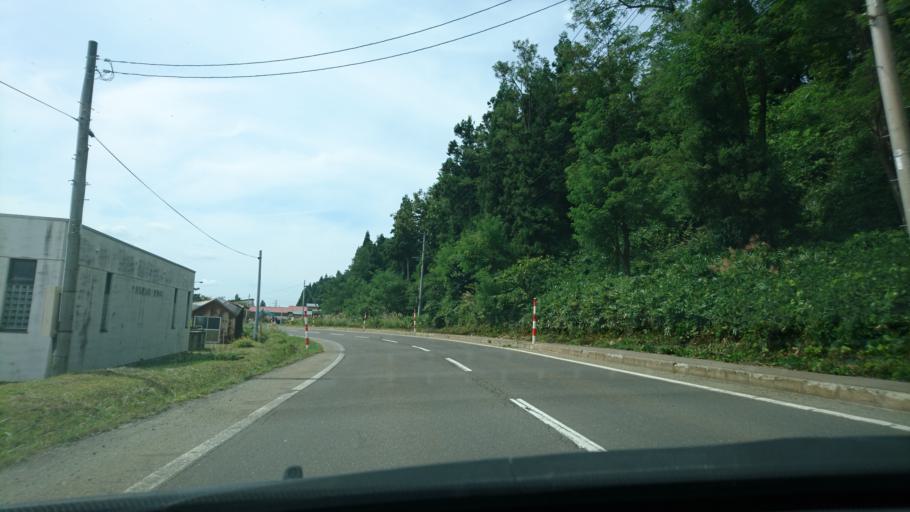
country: JP
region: Akita
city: Yuzawa
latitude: 39.2003
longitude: 140.5988
